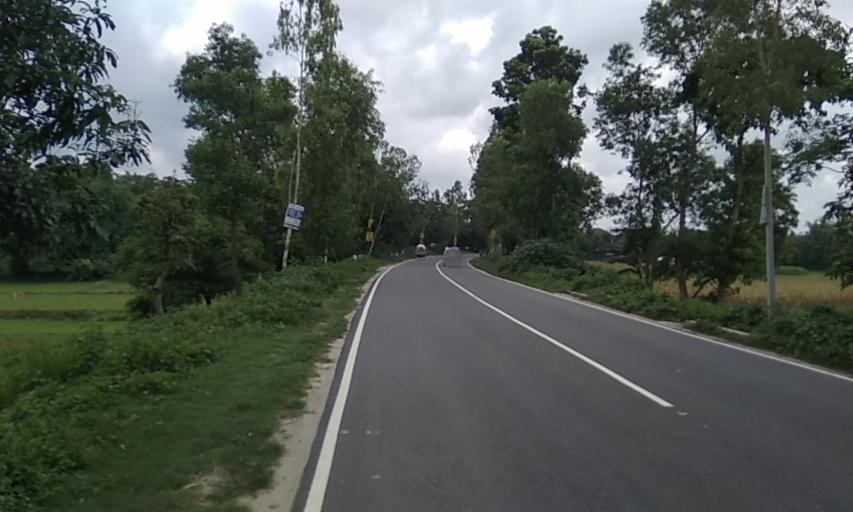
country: BD
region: Rangpur Division
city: Rangpur
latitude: 25.8015
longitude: 89.1868
